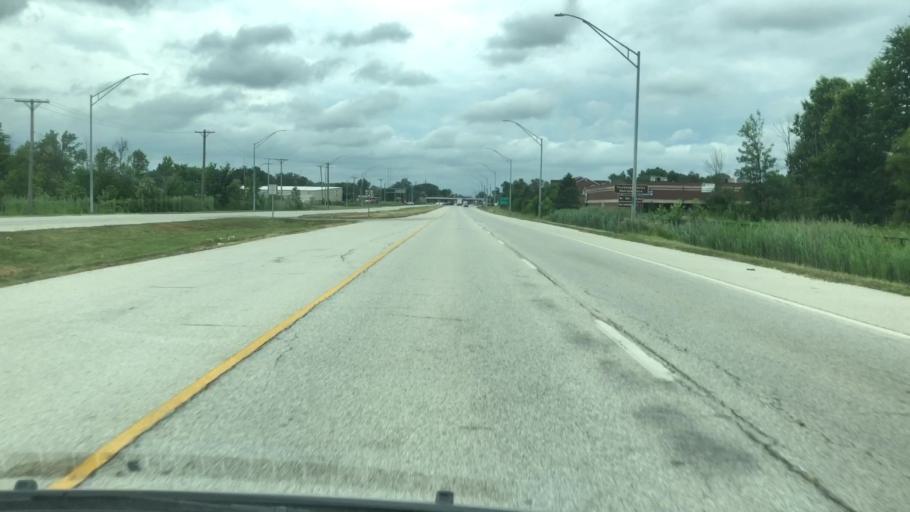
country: US
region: Ohio
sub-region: Summit County
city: Macedonia
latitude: 41.2947
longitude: -81.5124
